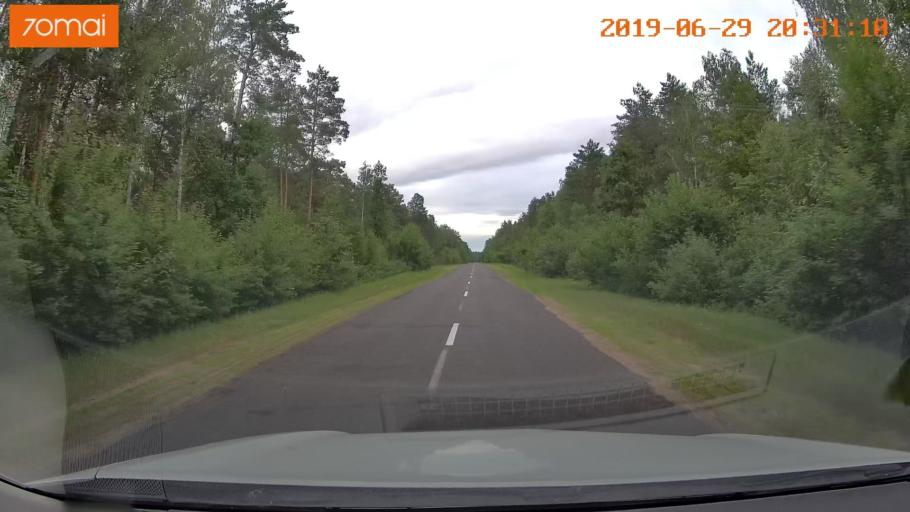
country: BY
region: Brest
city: Hantsavichy
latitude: 52.5117
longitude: 26.3396
